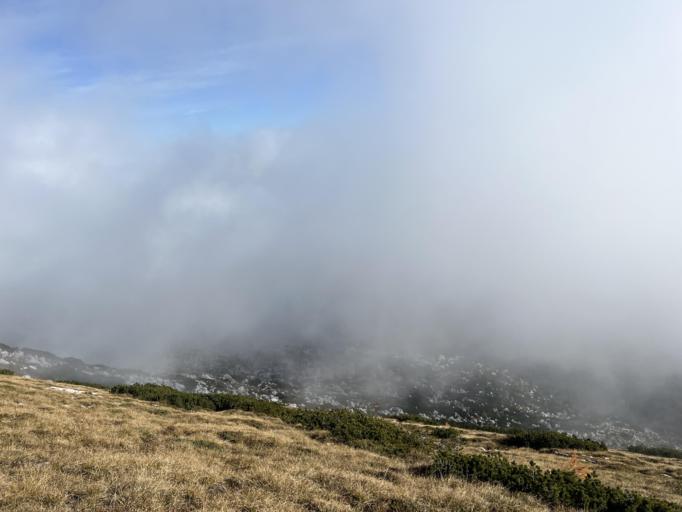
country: IT
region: Friuli Venezia Giulia
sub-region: Provincia di Pordenone
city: Andreis
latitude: 46.2195
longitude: 12.6524
